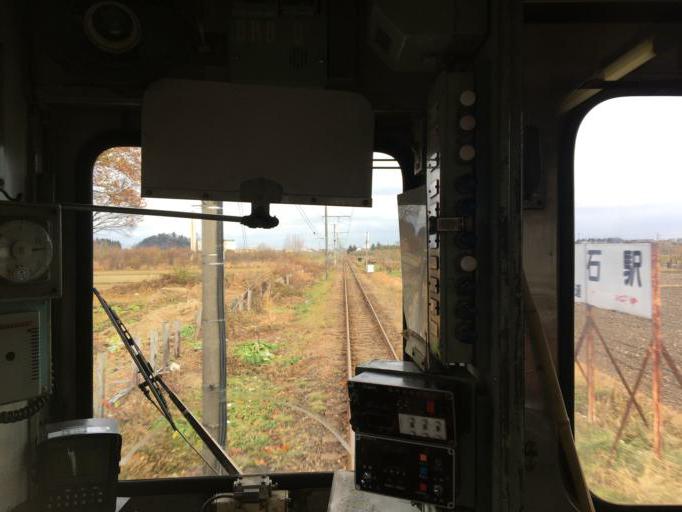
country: JP
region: Aomori
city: Hirosaki
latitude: 40.5367
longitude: 140.5525
